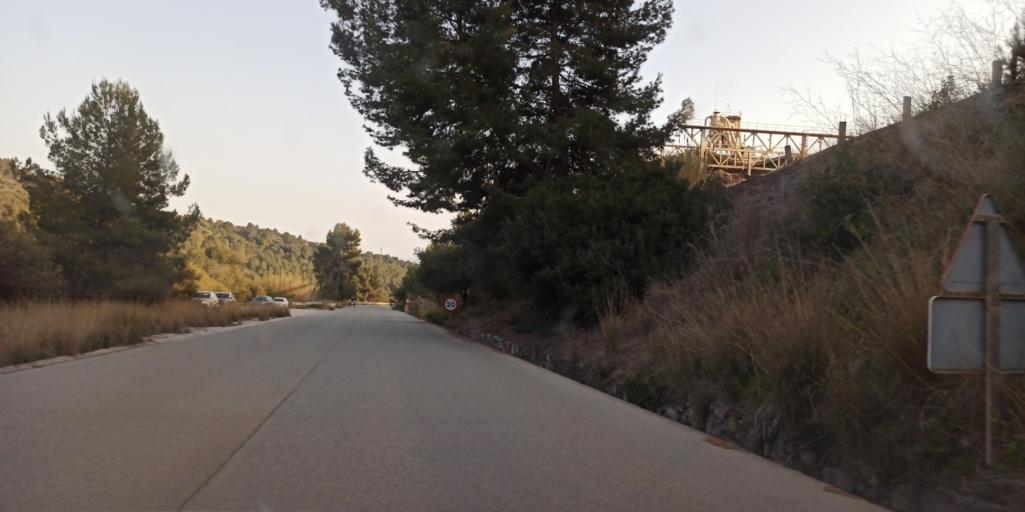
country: ES
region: Catalonia
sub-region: Provincia de Barcelona
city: Sant Feliu de Llobregat
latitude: 41.4034
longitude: 2.0556
